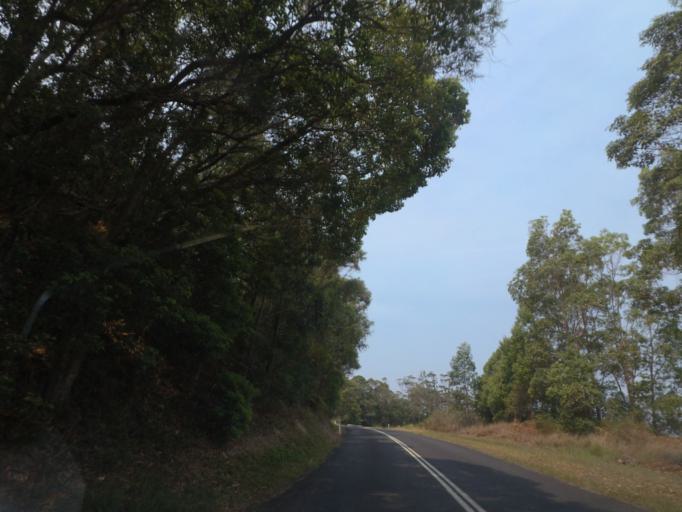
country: AU
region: New South Wales
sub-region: Tweed
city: Burringbar
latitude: -28.4538
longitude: 153.5311
